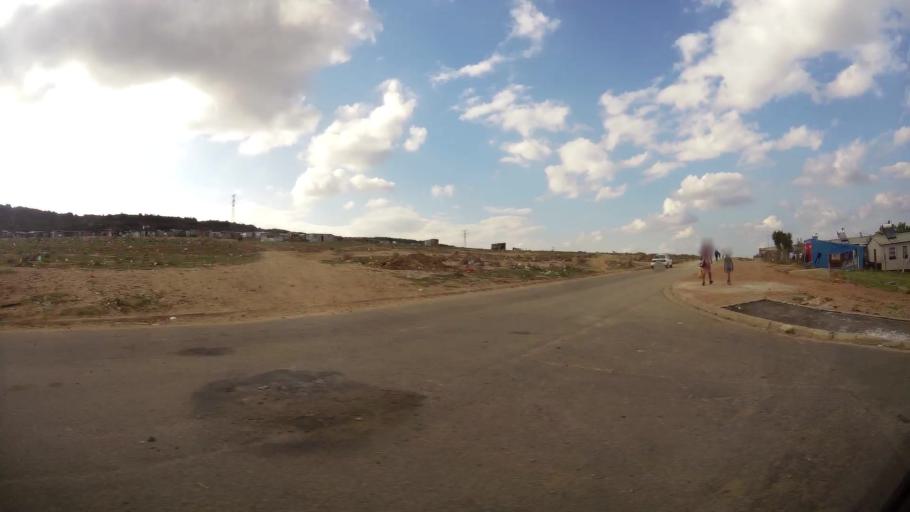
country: ZA
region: Eastern Cape
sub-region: Nelson Mandela Bay Metropolitan Municipality
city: Uitenhage
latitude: -33.7305
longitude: 25.3896
